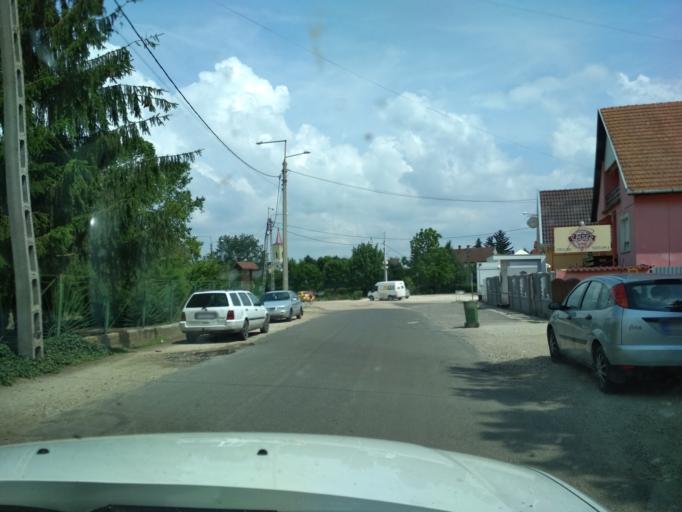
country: HU
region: Pest
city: Tapioszentmarton
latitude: 47.3404
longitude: 19.7444
